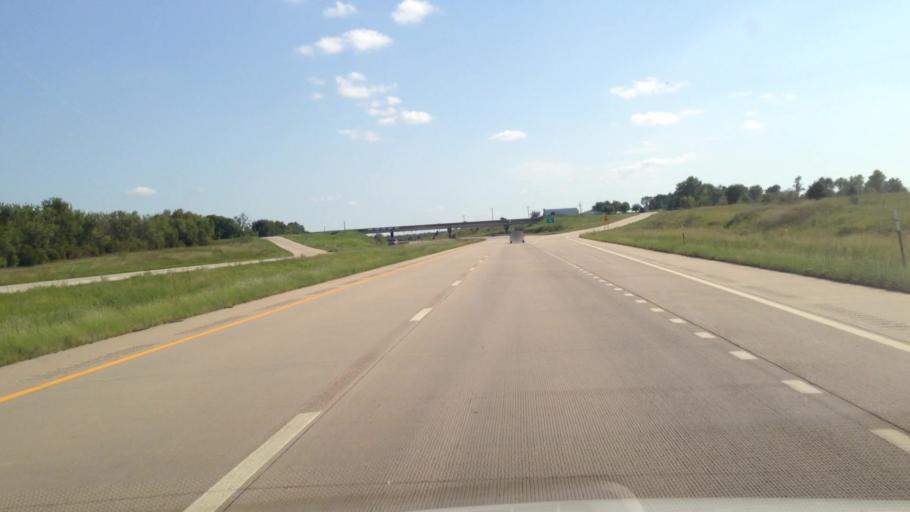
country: US
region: Kansas
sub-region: Bourbon County
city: Fort Scott
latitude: 37.8963
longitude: -94.7050
